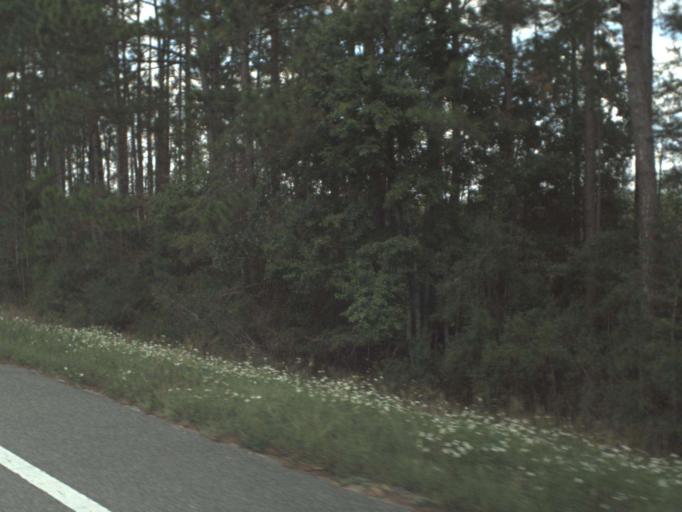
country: US
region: Florida
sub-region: Bay County
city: Laguna Beach
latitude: 30.4553
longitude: -85.9111
